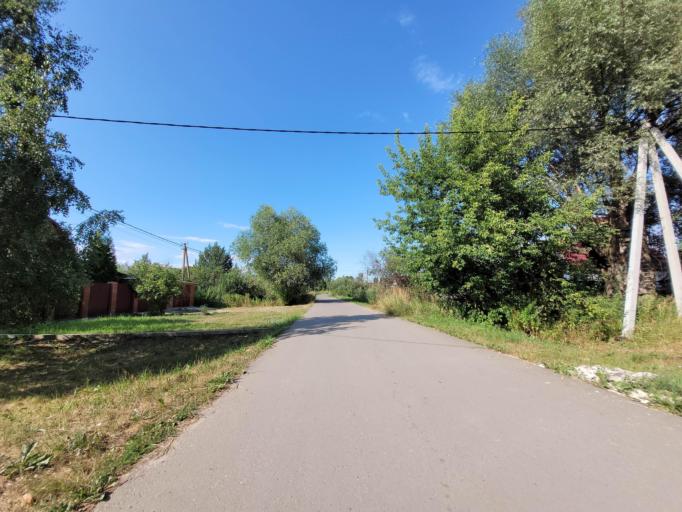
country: RU
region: Moskovskaya
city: Lopatinskiy
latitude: 55.3871
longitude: 38.7124
